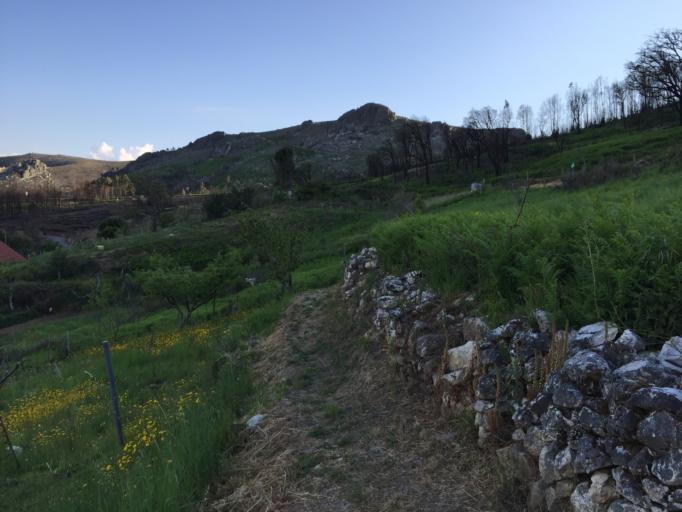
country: PT
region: Coimbra
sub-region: Pampilhosa da Serra
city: Pampilhosa da Serra
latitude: 40.1122
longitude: -7.8726
